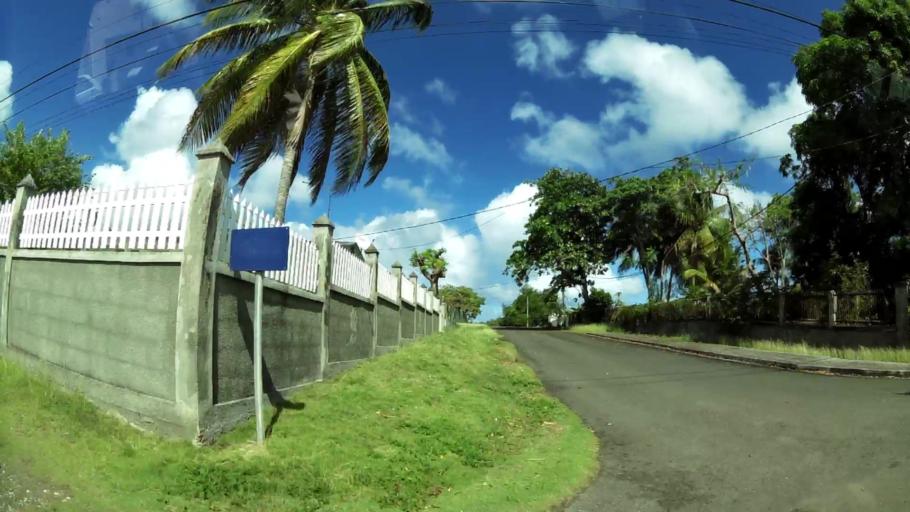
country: GP
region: Guadeloupe
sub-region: Guadeloupe
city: Anse-Bertrand
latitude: 16.4683
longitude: -61.5131
